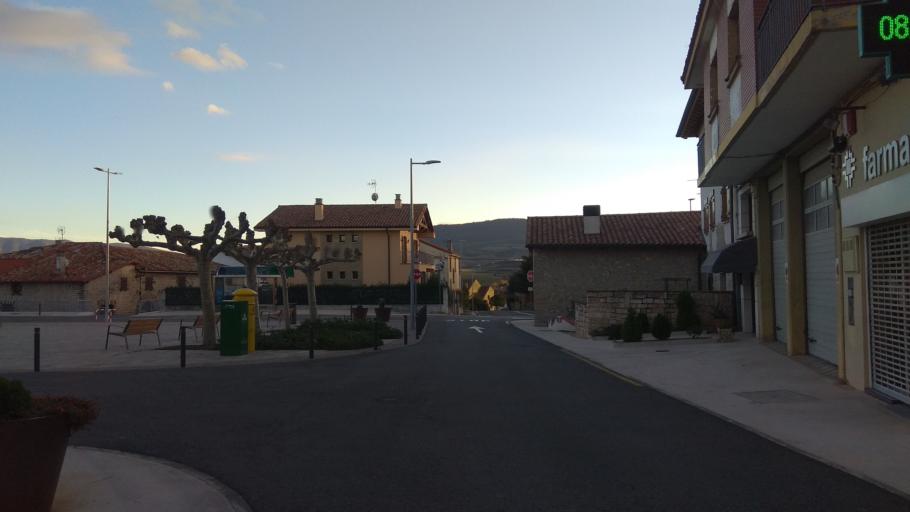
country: ES
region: Navarre
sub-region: Provincia de Navarra
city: Cizur Mayor
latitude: 42.7934
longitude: -1.6950
